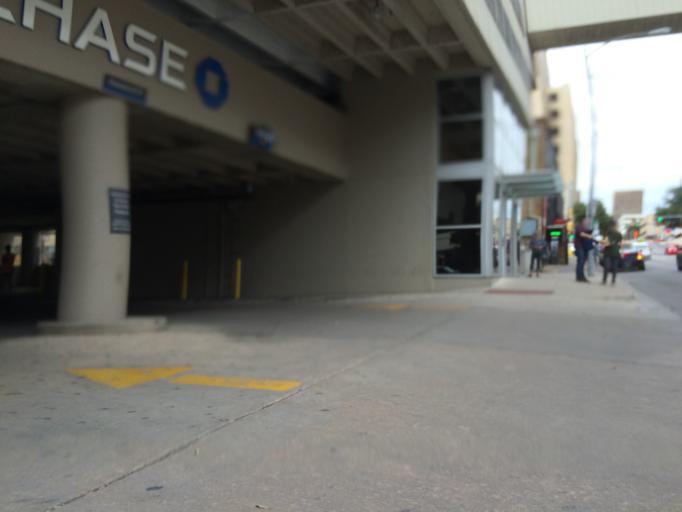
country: US
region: Texas
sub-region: Travis County
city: Austin
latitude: 30.2680
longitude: -97.7456
